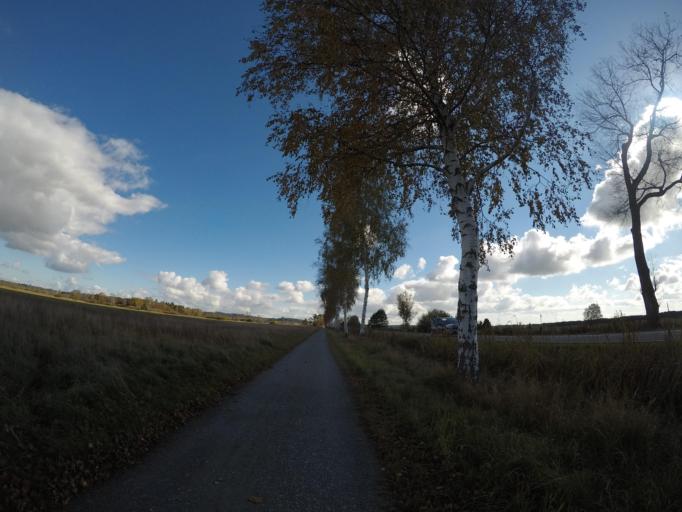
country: DE
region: Baden-Wuerttemberg
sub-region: Tuebingen Region
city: Bad Buchau
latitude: 48.0656
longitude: 9.6237
